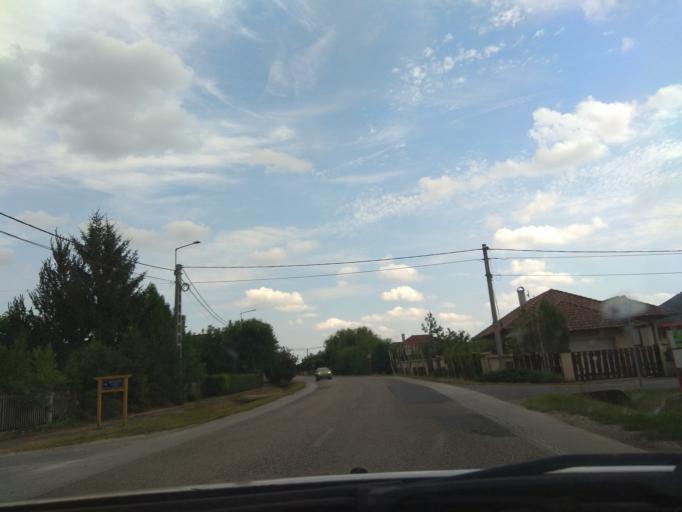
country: HU
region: Borsod-Abauj-Zemplen
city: Malyi
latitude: 48.0400
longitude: 20.8425
